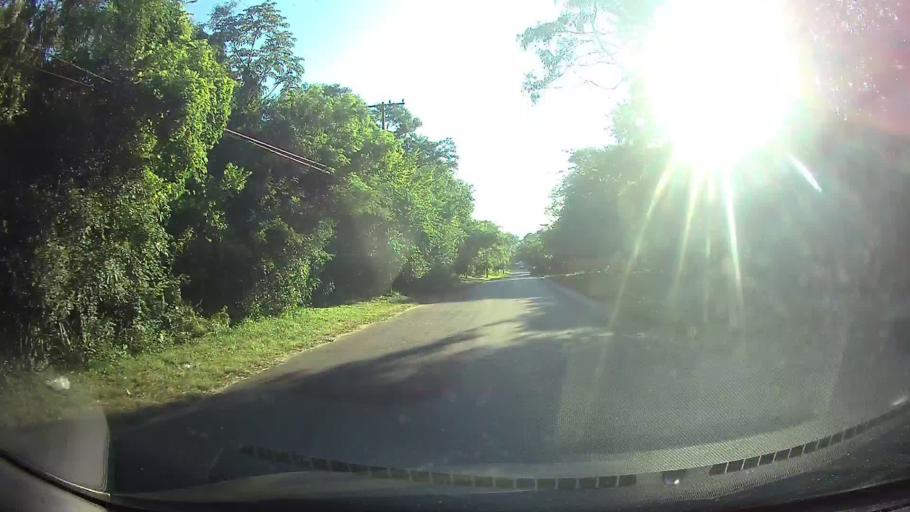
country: PY
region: Cordillera
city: San Bernardino
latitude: -25.3181
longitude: -57.2696
